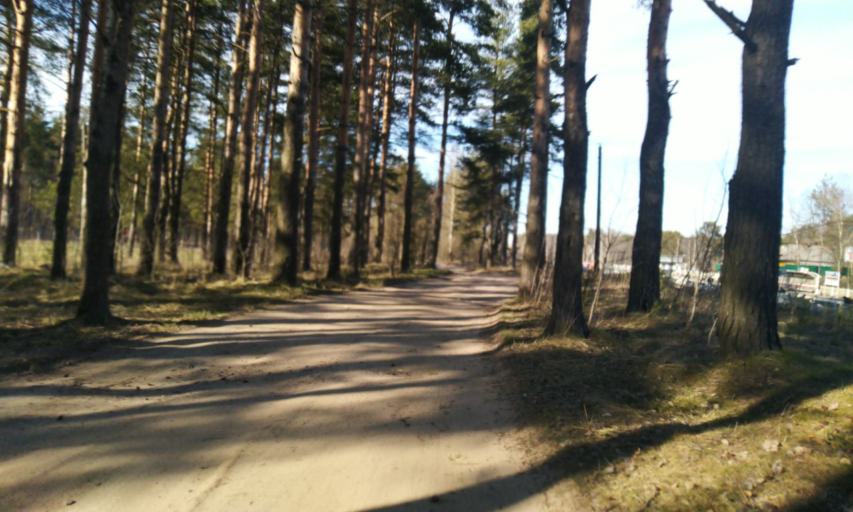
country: RU
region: Leningrad
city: Novoye Devyatkino
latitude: 60.1117
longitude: 30.4829
